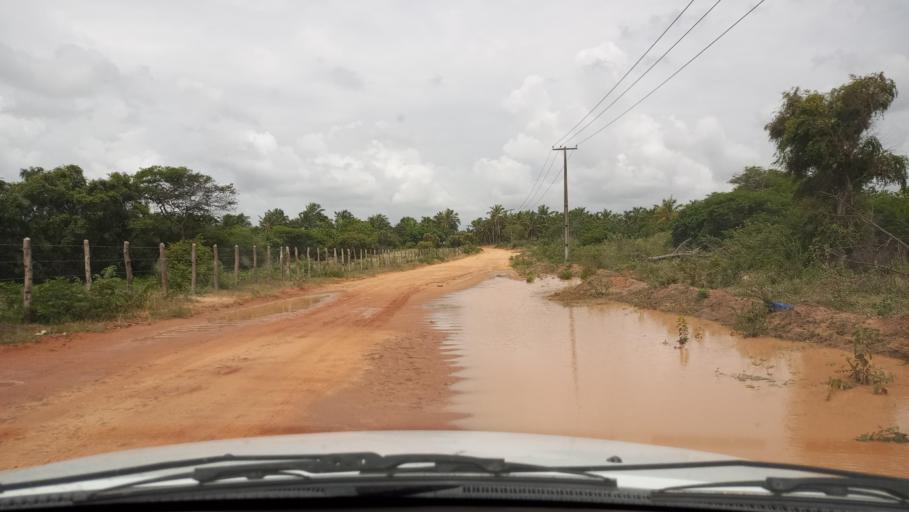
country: BR
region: Rio Grande do Norte
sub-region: Maxaranguape
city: Sao Miguel
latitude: -5.4841
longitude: -35.3124
